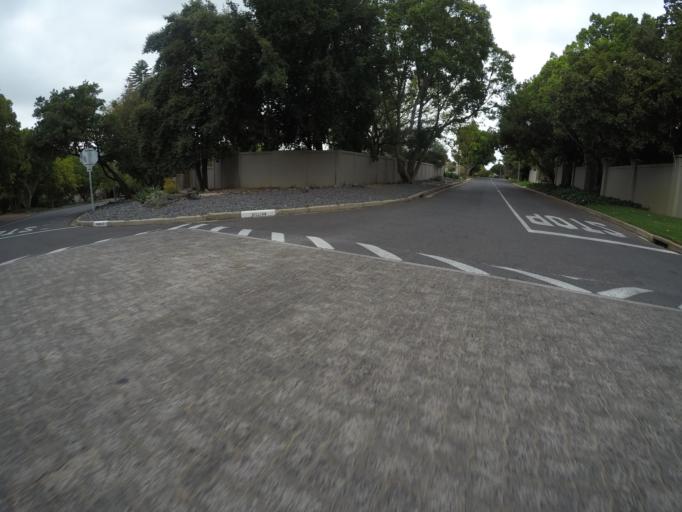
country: ZA
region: Western Cape
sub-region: City of Cape Town
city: Kraaifontein
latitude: -33.8637
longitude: 18.6480
